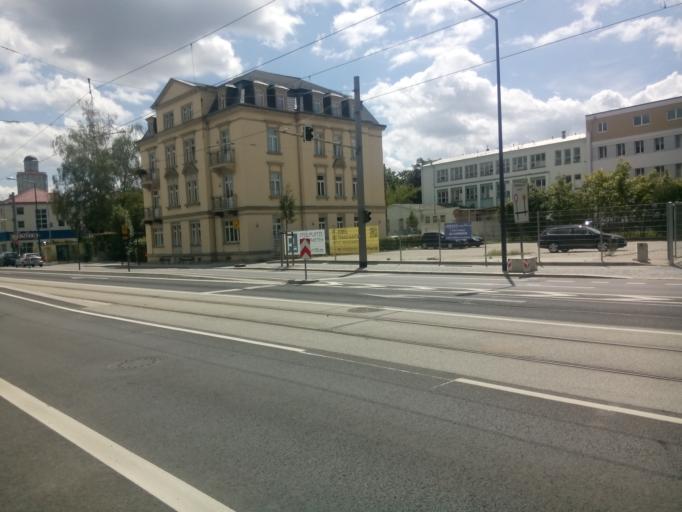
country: DE
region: Saxony
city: Albertstadt
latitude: 51.0430
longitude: 13.7939
